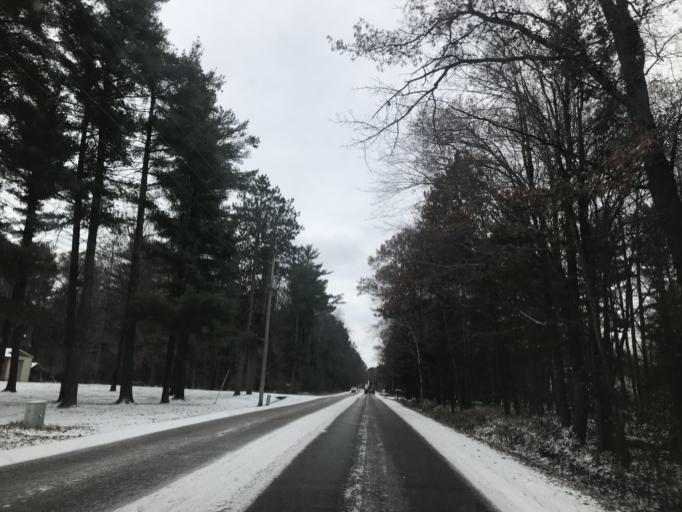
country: US
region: Wisconsin
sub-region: Marinette County
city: Marinette
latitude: 45.0679
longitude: -87.6594
